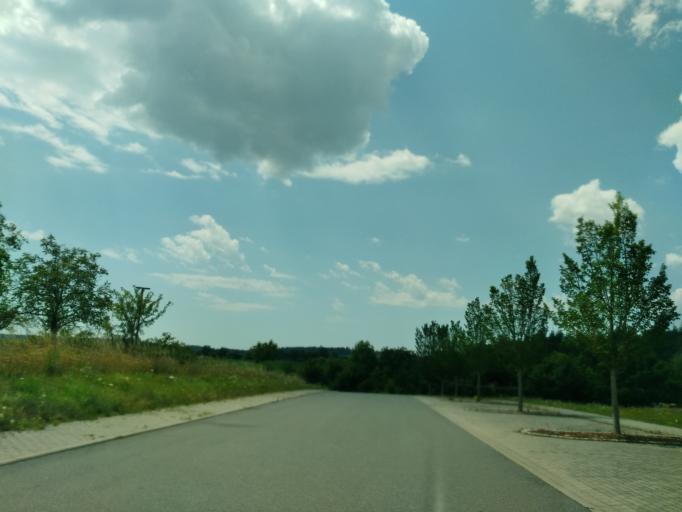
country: DE
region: Baden-Wuerttemberg
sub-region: Karlsruhe Region
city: Seckach
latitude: 49.4487
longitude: 9.2830
